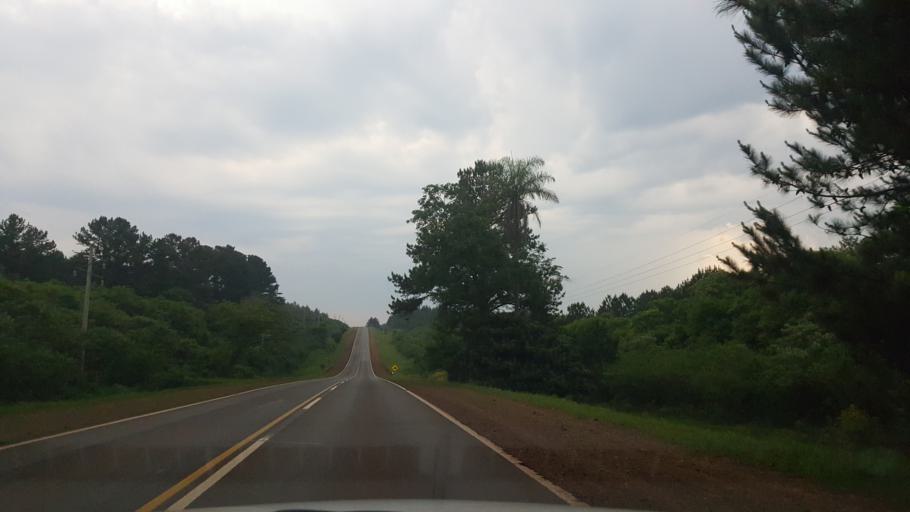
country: AR
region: Misiones
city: Jardin America
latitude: -27.0230
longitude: -55.2047
